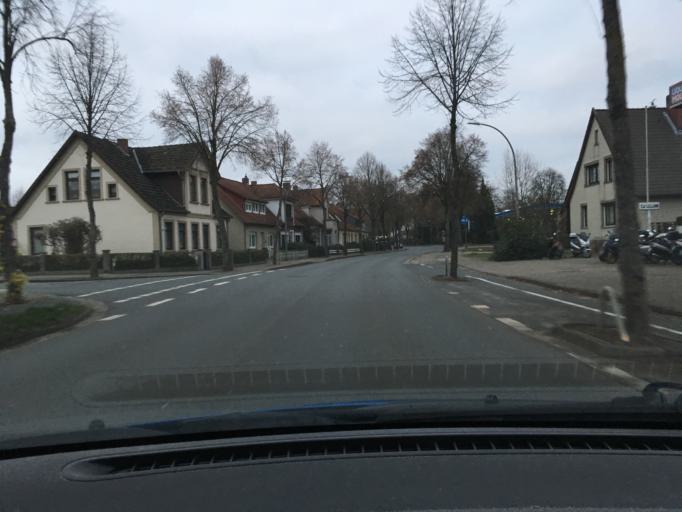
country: DE
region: Lower Saxony
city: Walsrode
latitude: 52.8537
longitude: 9.5966
